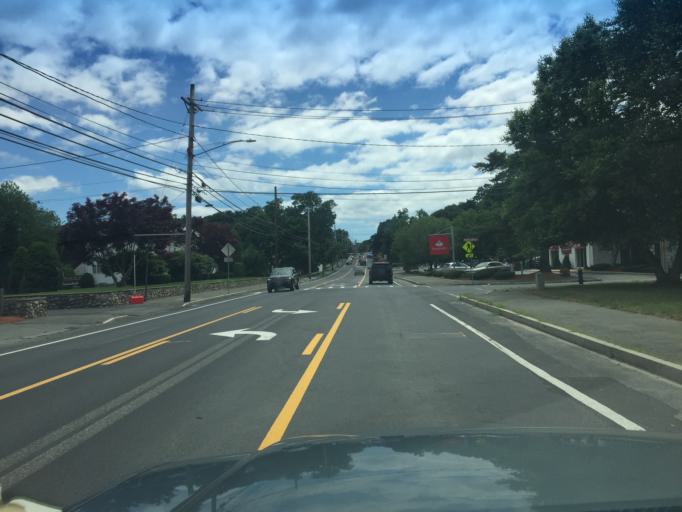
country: US
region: Massachusetts
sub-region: Middlesex County
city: Reading
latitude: 42.5134
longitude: -71.1039
